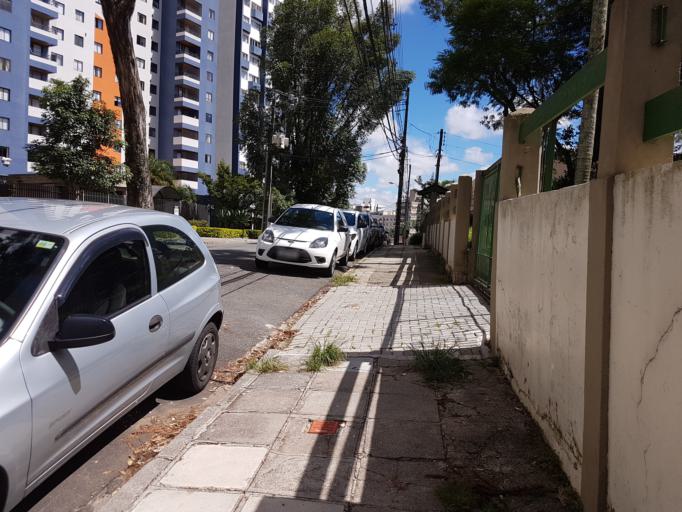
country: BR
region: Parana
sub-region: Curitiba
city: Curitiba
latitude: -25.4361
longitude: -49.2413
